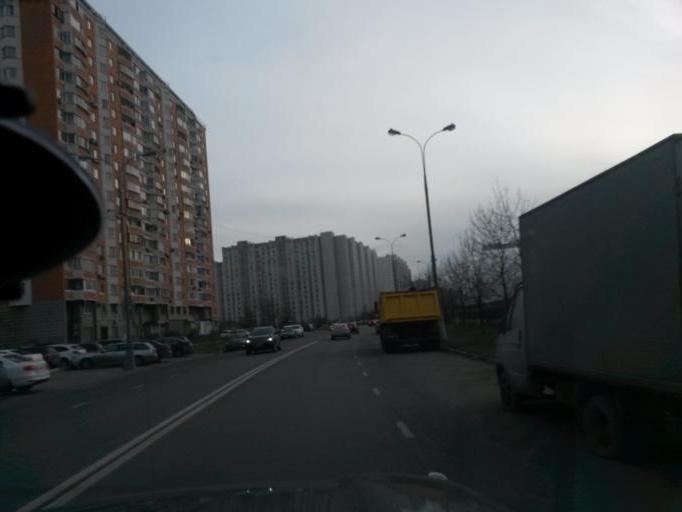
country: RU
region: Moscow
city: Brateyevo
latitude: 55.6599
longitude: 37.7712
